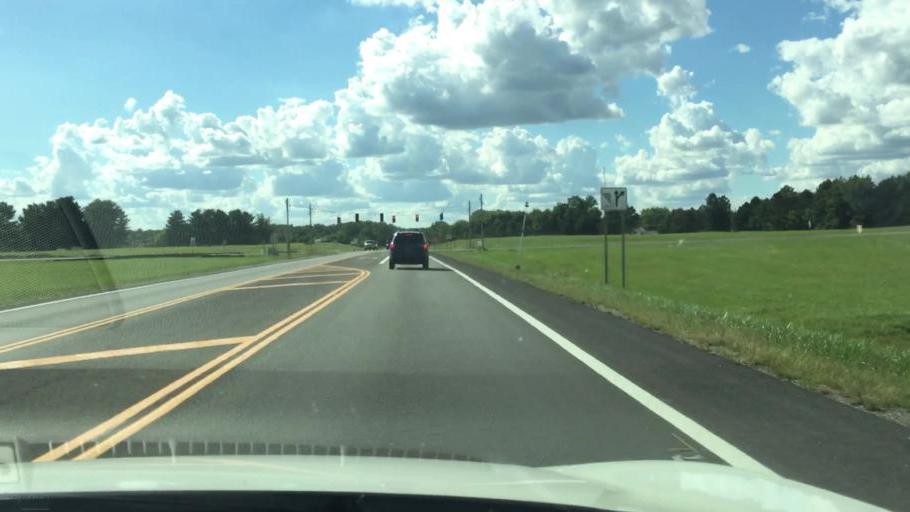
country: US
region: Ohio
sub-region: Clark County
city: Northridge
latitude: 39.9774
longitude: -83.7630
